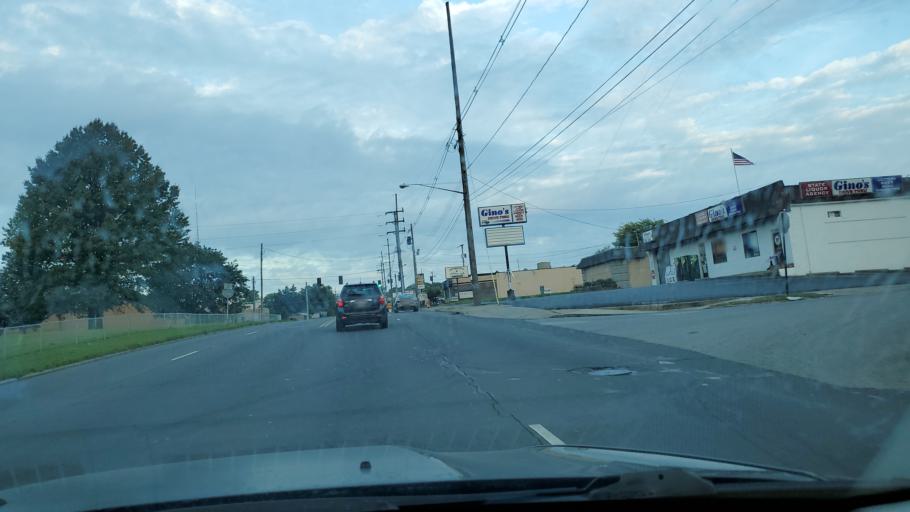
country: US
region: Ohio
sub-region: Mahoning County
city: Struthers
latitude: 41.0608
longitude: -80.6337
